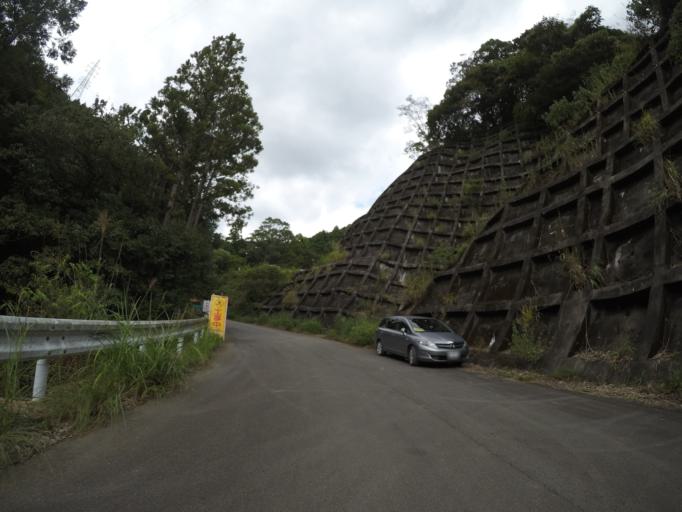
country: JP
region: Shizuoka
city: Shimada
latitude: 34.8818
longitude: 138.1725
